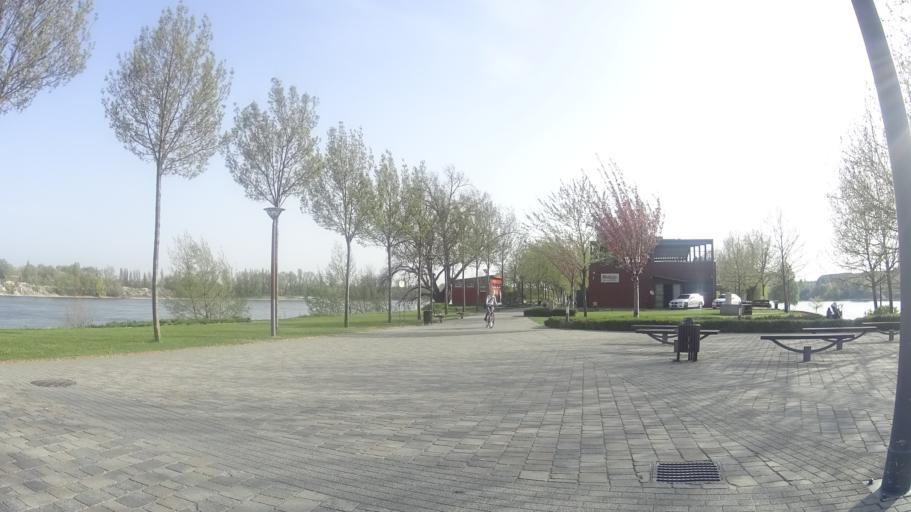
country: HU
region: Budapest
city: Budapest IX. keruelet
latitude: 47.4663
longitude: 19.0639
